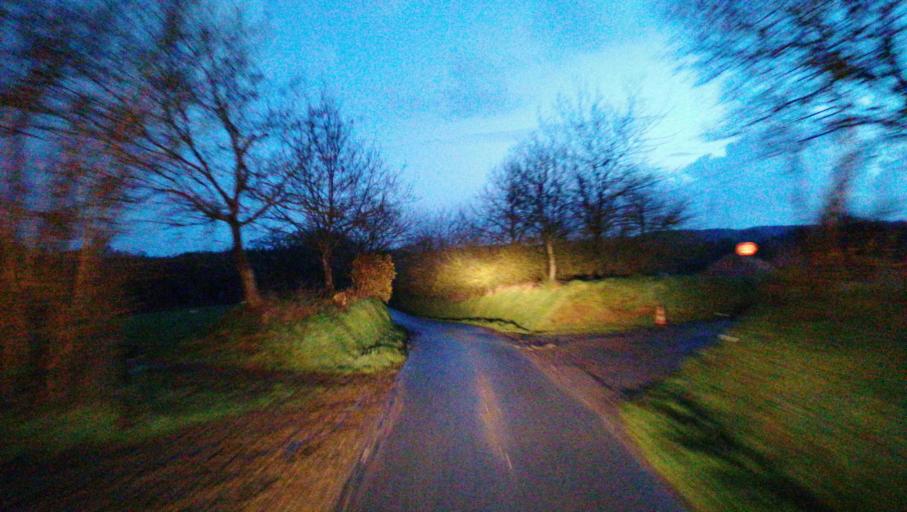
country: FR
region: Brittany
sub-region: Departement des Cotes-d'Armor
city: Plehedel
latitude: 48.6700
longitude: -3.0506
